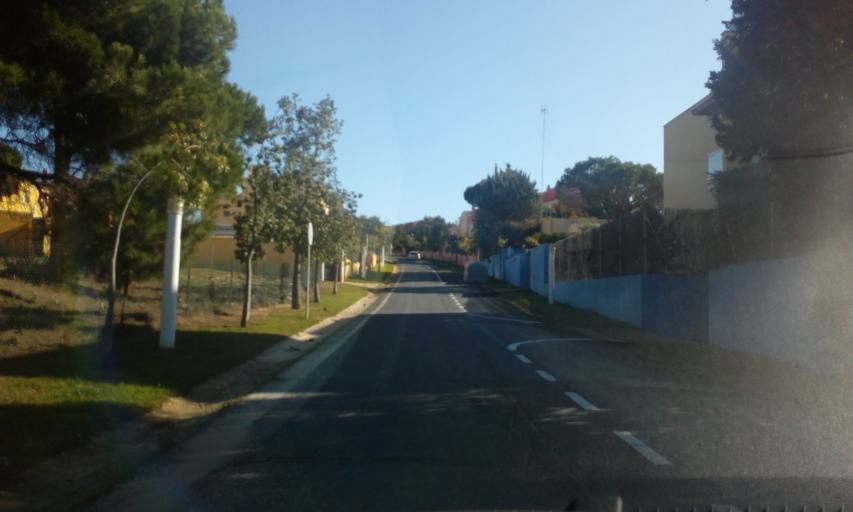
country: ES
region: Andalusia
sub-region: Provincia de Huelva
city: Lepe
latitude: 37.2101
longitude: -7.2432
